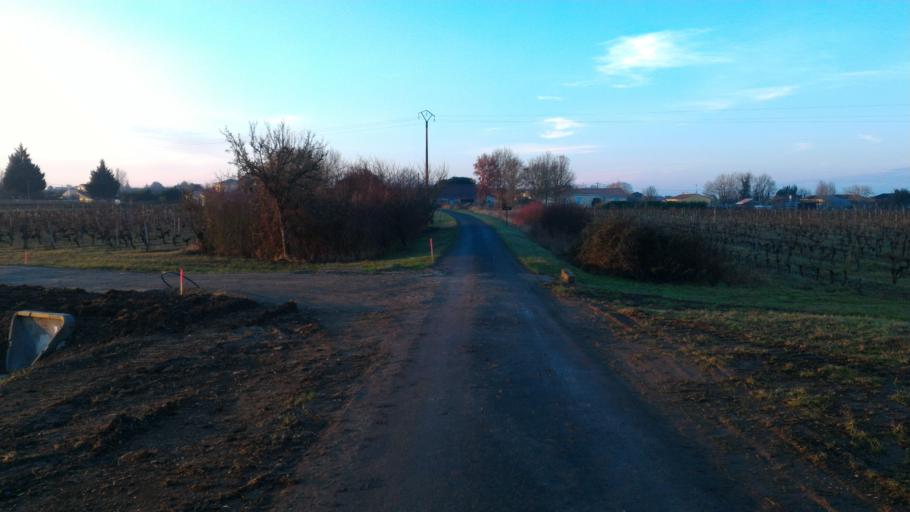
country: FR
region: Aquitaine
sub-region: Departement de la Gironde
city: Saint-Martin-Lacaussade
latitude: 45.1645
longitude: -0.6490
